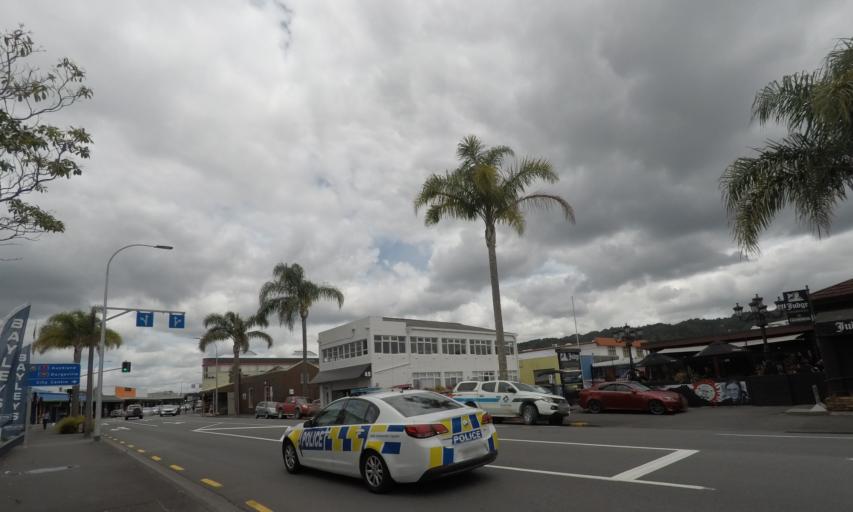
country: NZ
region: Northland
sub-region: Whangarei
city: Whangarei
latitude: -35.7261
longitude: 174.3227
